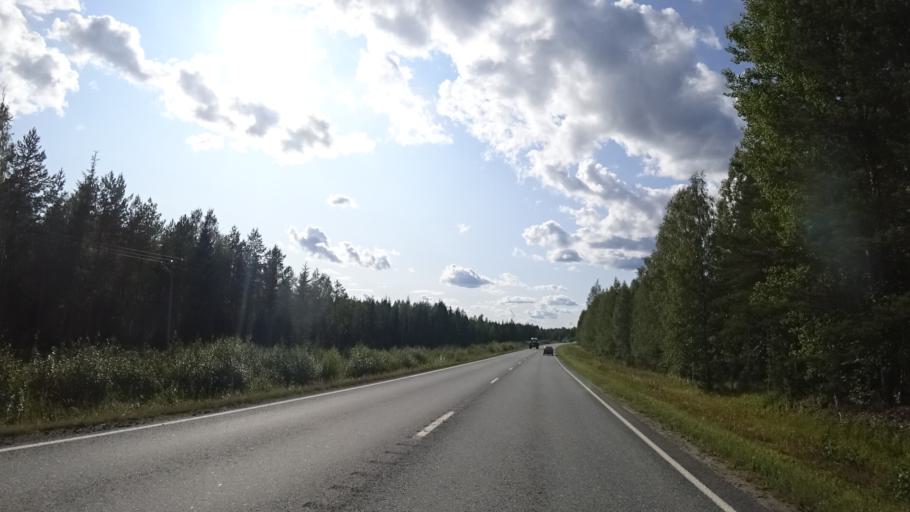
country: FI
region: North Karelia
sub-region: Keski-Karjala
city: Kitee
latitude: 62.0884
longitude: 29.9937
